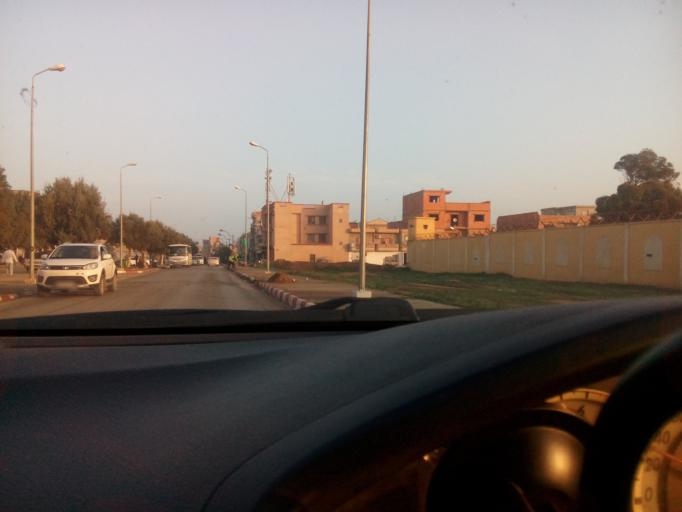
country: DZ
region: Oran
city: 'Ain el Turk
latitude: 35.7366
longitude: -0.7724
